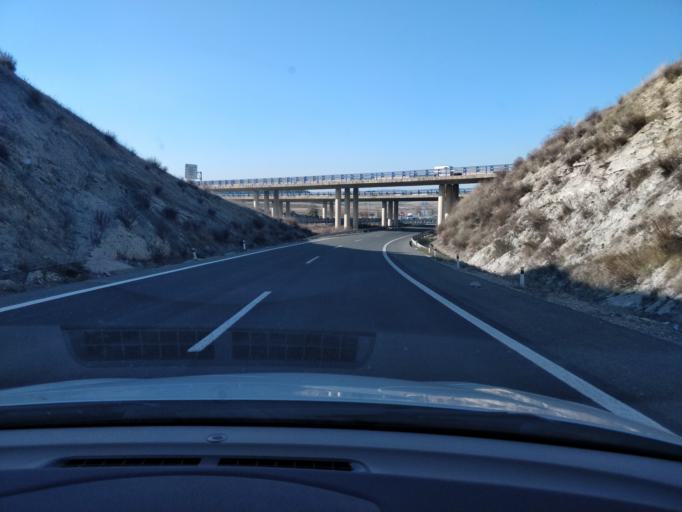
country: ES
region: Basque Country
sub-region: Provincia de Alava
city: Arminon
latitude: 42.7096
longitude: -2.9023
